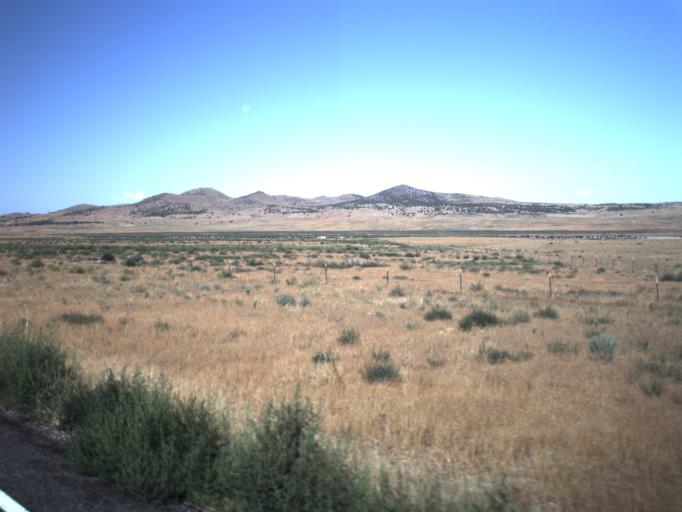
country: US
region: Utah
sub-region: Juab County
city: Nephi
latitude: 39.6916
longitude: -112.2344
